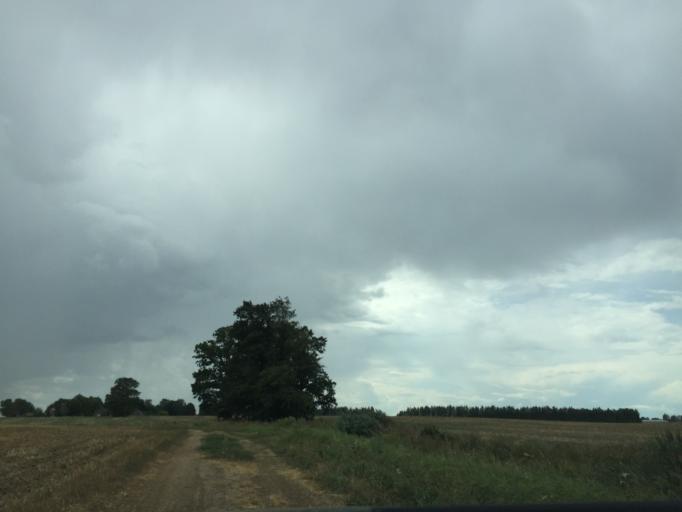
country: LT
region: Siauliu apskritis
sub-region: Joniskis
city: Joniskis
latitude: 56.2918
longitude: 23.7260
